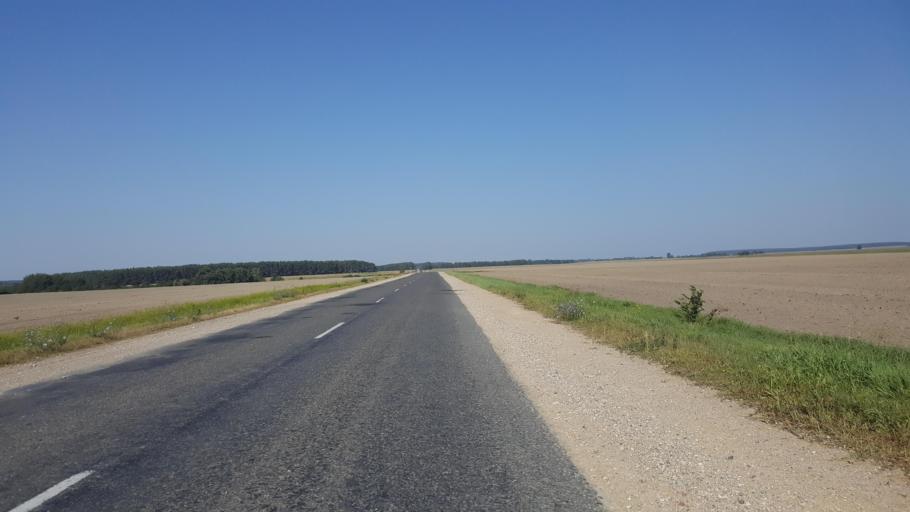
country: BY
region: Brest
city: Kamyanyets
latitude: 52.4038
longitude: 23.7607
